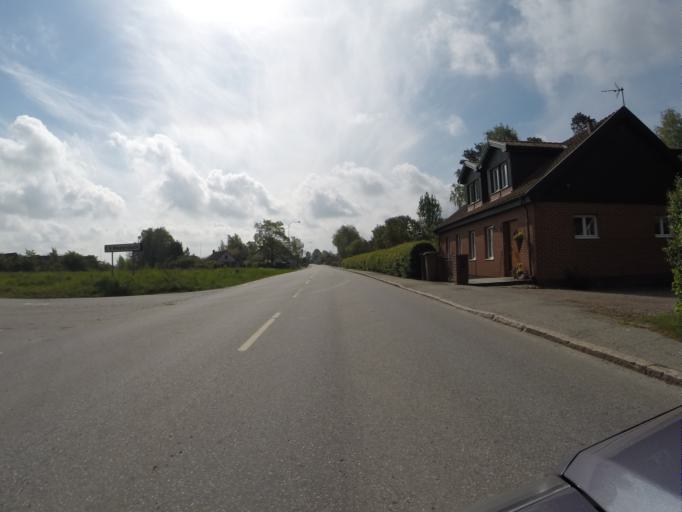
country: SE
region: Skane
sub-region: Svalovs Kommun
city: Teckomatorp
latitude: 55.8397
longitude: 13.0176
